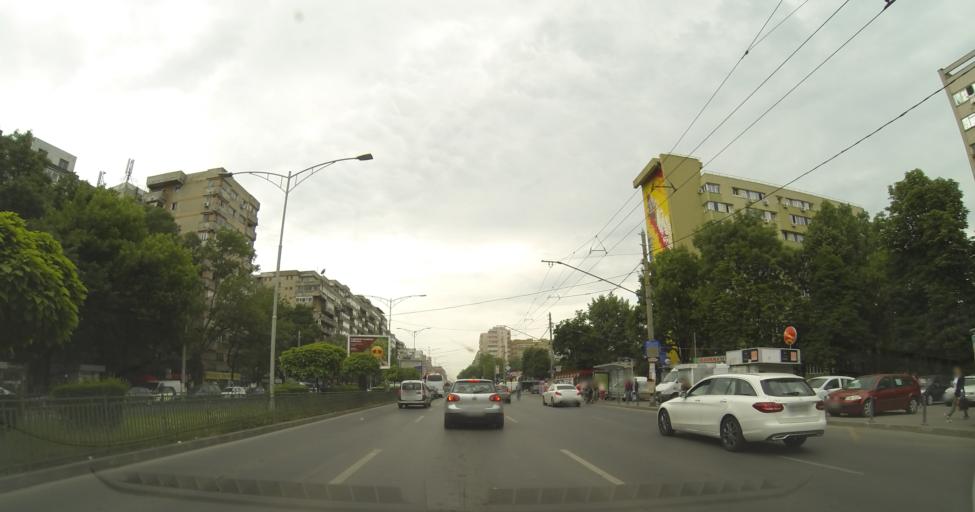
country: RO
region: Ilfov
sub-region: Comuna Chiajna
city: Rosu
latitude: 44.4341
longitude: 26.0220
